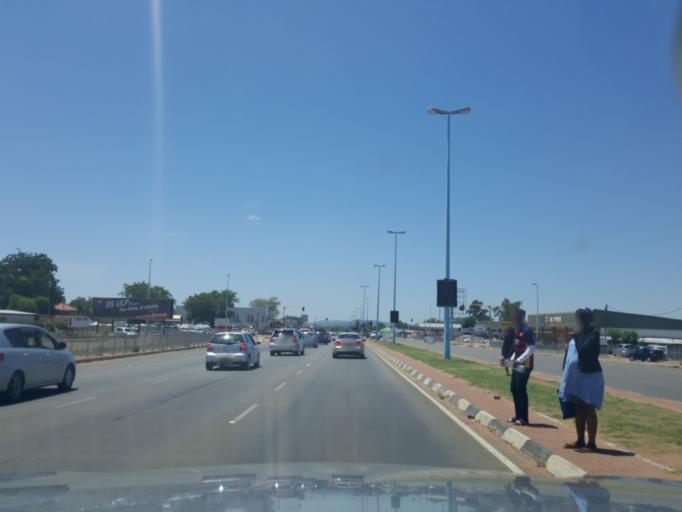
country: BW
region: Kweneng
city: Mogoditshane
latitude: -24.6276
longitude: 25.8710
